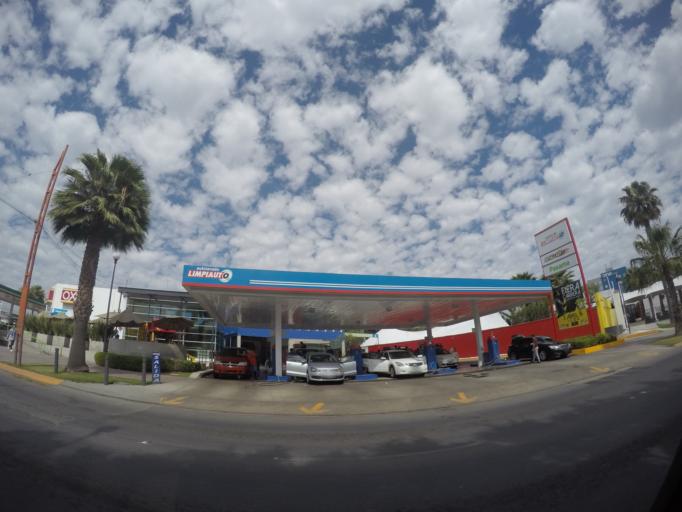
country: MX
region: Guanajuato
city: Leon
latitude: 21.1047
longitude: -101.6590
